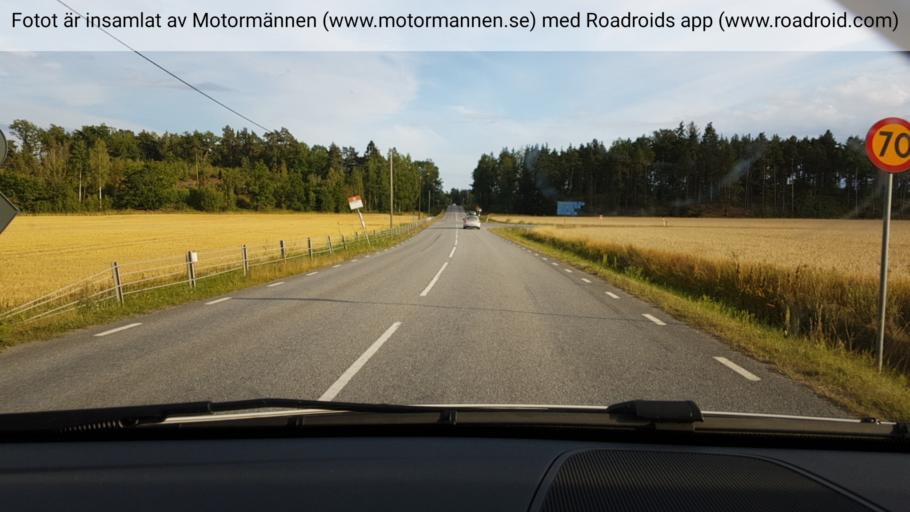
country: SE
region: Stockholm
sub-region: Sigtuna Kommun
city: Sigtuna
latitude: 59.6599
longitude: 17.6901
